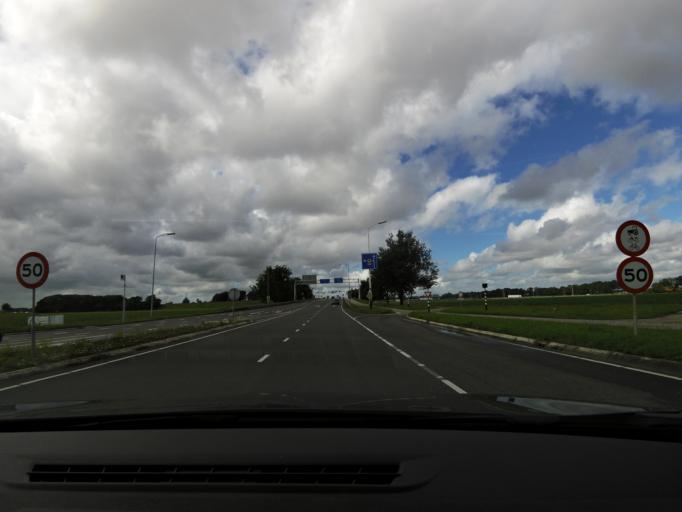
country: NL
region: South Holland
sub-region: Gemeente Binnenmaas
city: Mijnsheerenland
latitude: 51.8142
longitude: 4.4949
